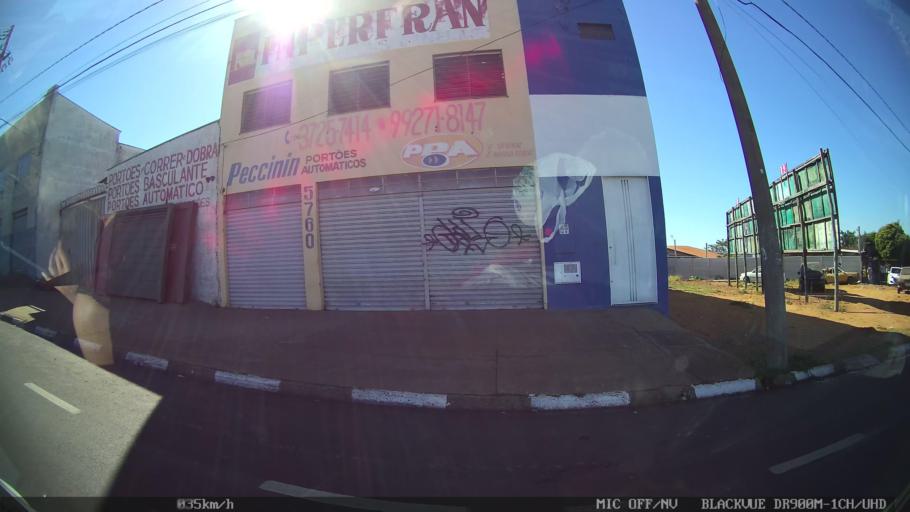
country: BR
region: Sao Paulo
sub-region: Franca
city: Franca
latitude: -20.5435
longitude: -47.3590
